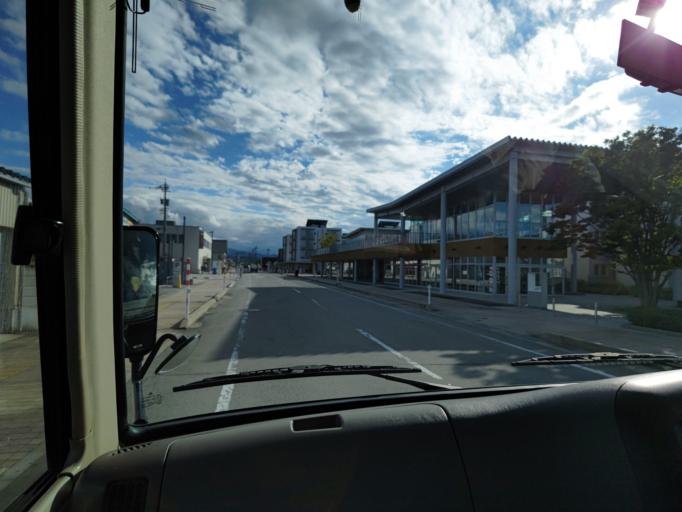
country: JP
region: Toyama
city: Nyuzen
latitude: 36.8791
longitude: 137.4465
